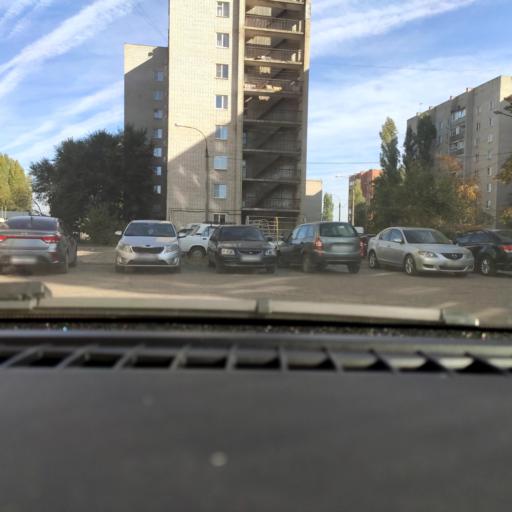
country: RU
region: Voronezj
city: Voronezh
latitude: 51.6421
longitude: 39.2737
